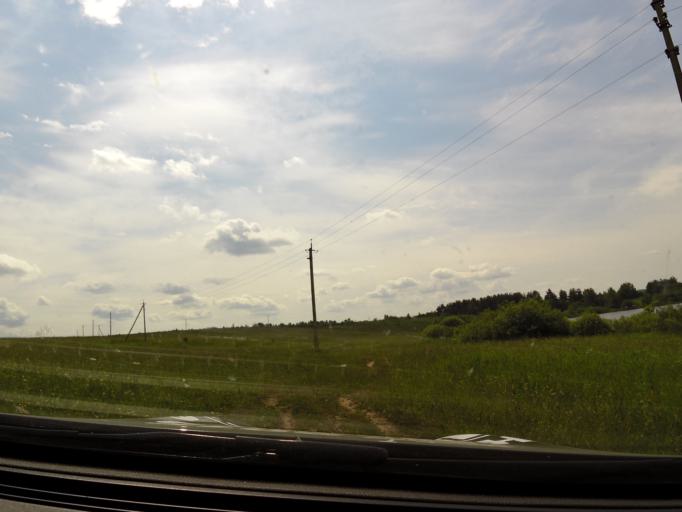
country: RU
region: Kostroma
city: Galich
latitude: 58.3759
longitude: 42.3973
